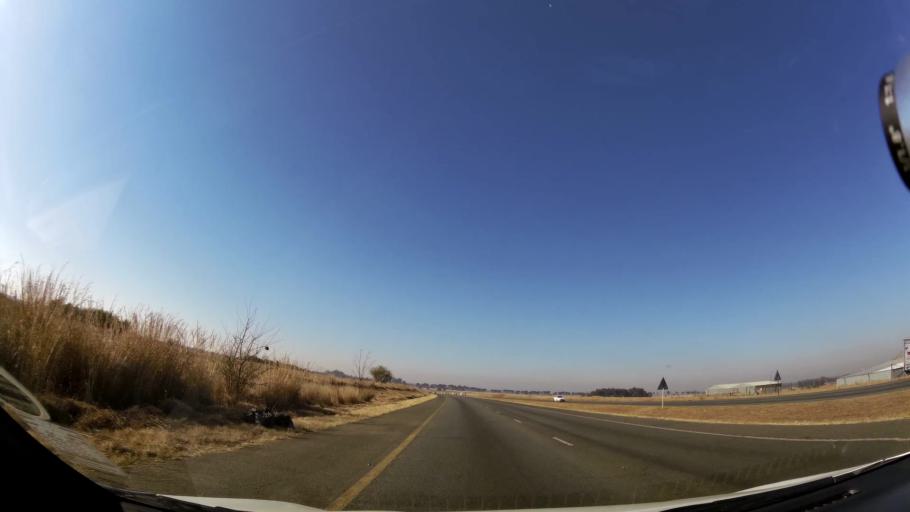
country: ZA
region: Gauteng
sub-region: City of Johannesburg Metropolitan Municipality
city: Johannesburg
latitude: -26.3252
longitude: 28.0692
